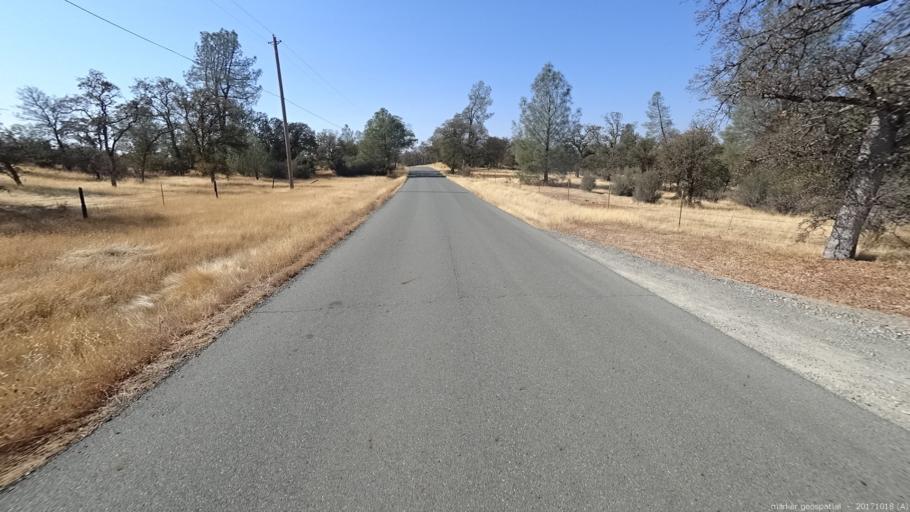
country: US
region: California
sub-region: Shasta County
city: Palo Cedro
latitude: 40.5413
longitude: -122.1110
